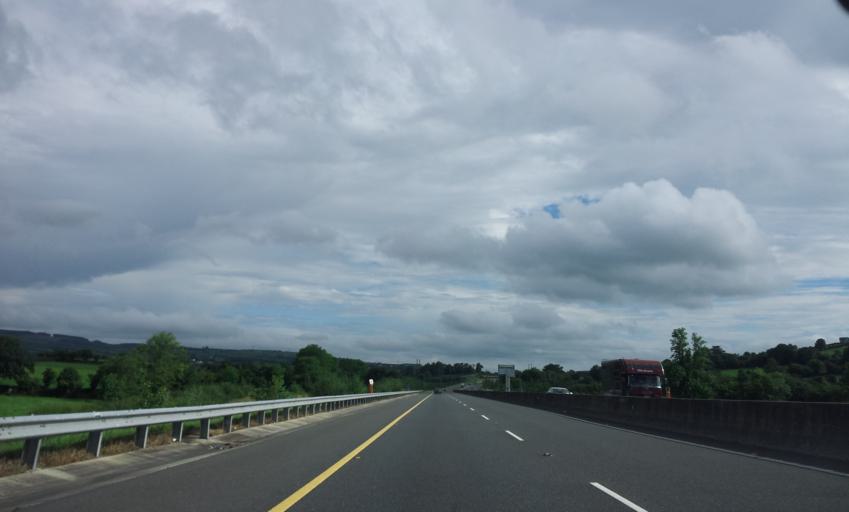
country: IE
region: Munster
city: Ballina
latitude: 52.7750
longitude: -8.3803
